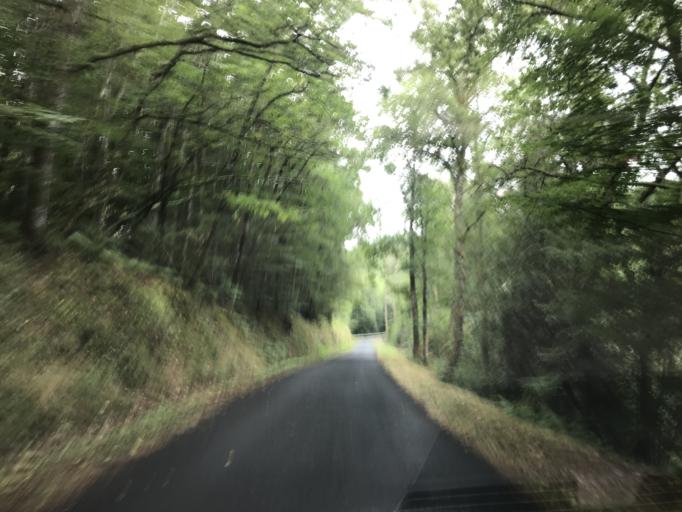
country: FR
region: Limousin
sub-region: Departement de la Correze
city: Saint-Privat
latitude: 45.2020
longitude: 2.1577
